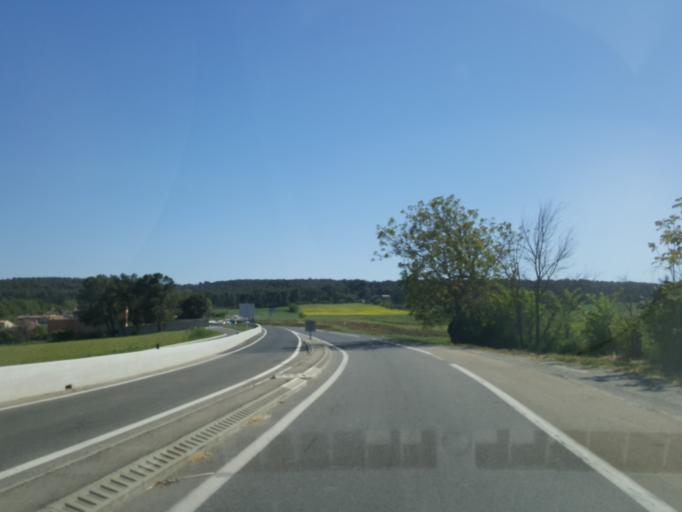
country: FR
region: Provence-Alpes-Cote d'Azur
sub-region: Departement des Bouches-du-Rhone
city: Cabries
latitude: 43.4454
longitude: 5.3607
